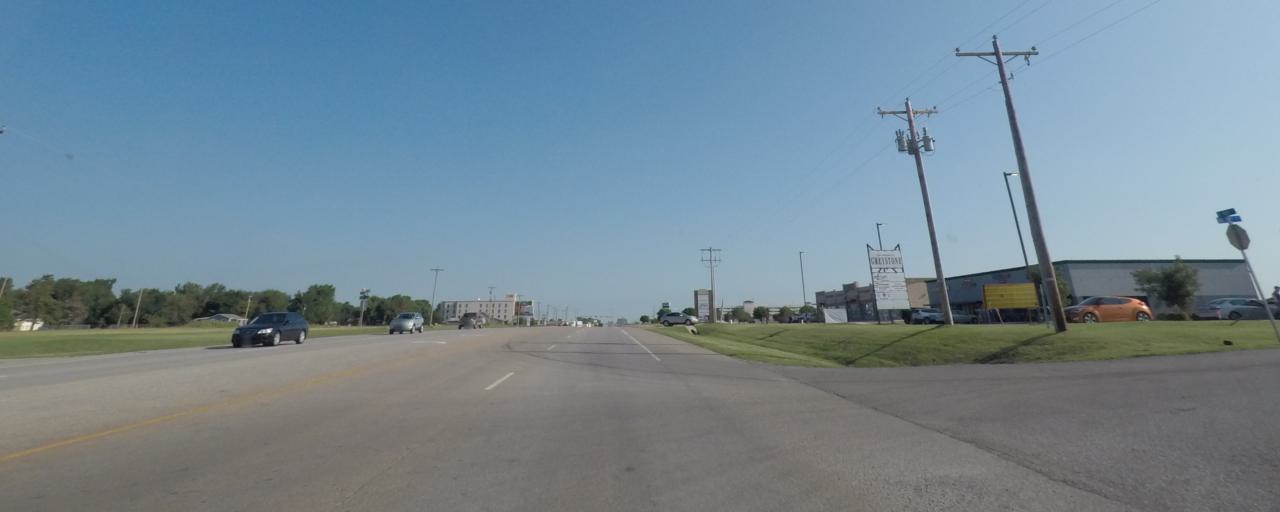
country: US
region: Oklahoma
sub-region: McClain County
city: Newcastle
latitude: 35.2713
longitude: -97.6001
